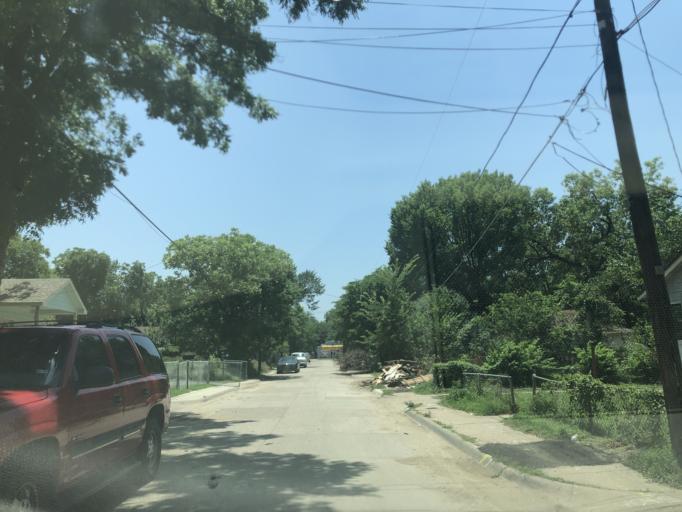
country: US
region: Texas
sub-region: Dallas County
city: Dallas
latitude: 32.7847
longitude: -96.8443
